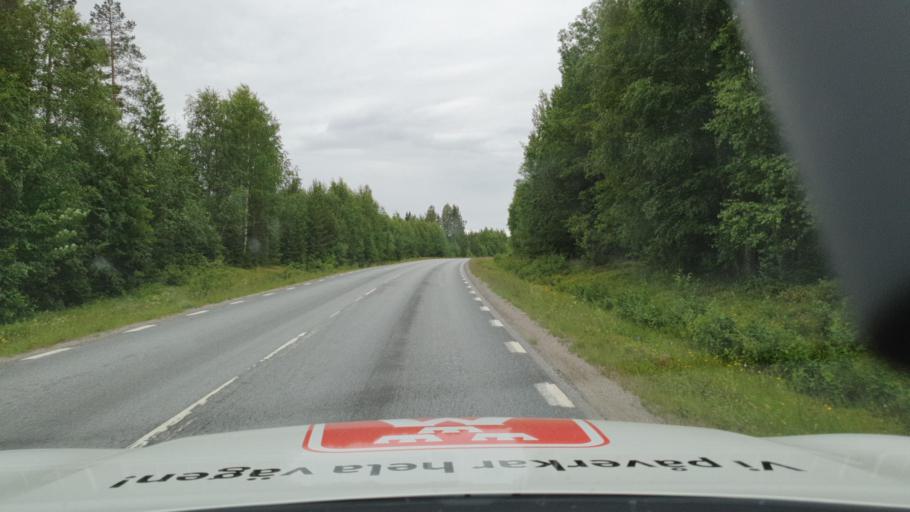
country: SE
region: Vaesterbotten
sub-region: Vannas Kommun
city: Vaennaes
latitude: 63.7730
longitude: 19.7204
